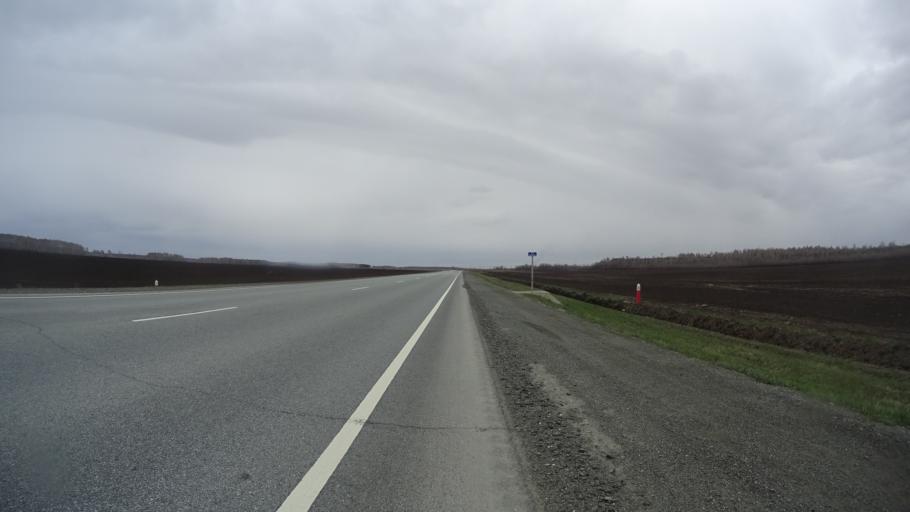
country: RU
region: Chelyabinsk
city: Krasnogorskiy
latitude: 54.5722
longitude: 61.2907
